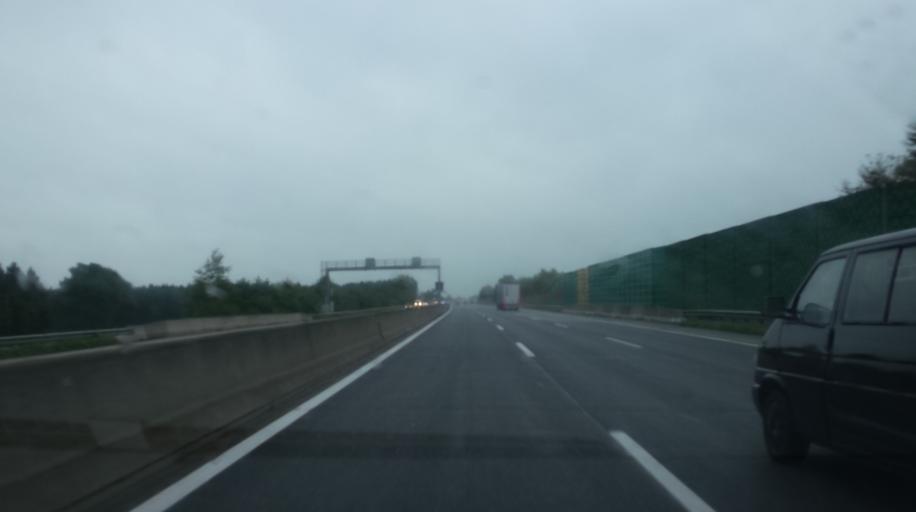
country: AT
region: Lower Austria
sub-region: Politischer Bezirk Amstetten
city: Wolfsbach
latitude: 48.1137
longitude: 14.6955
